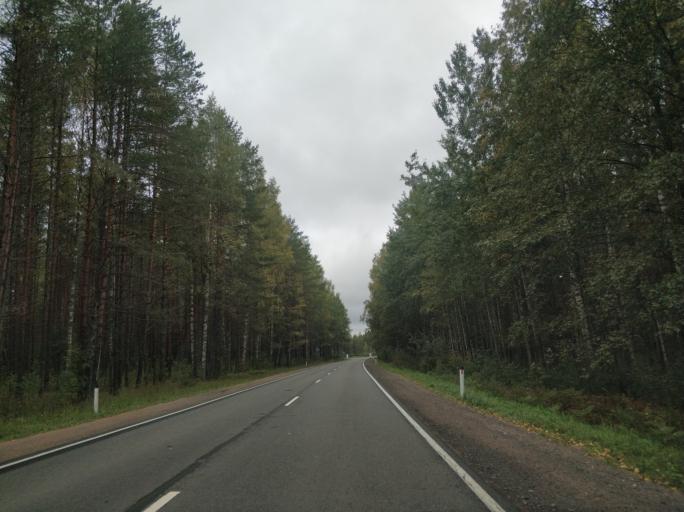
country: RU
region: Leningrad
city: Borisova Griva
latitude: 60.0907
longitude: 30.8592
